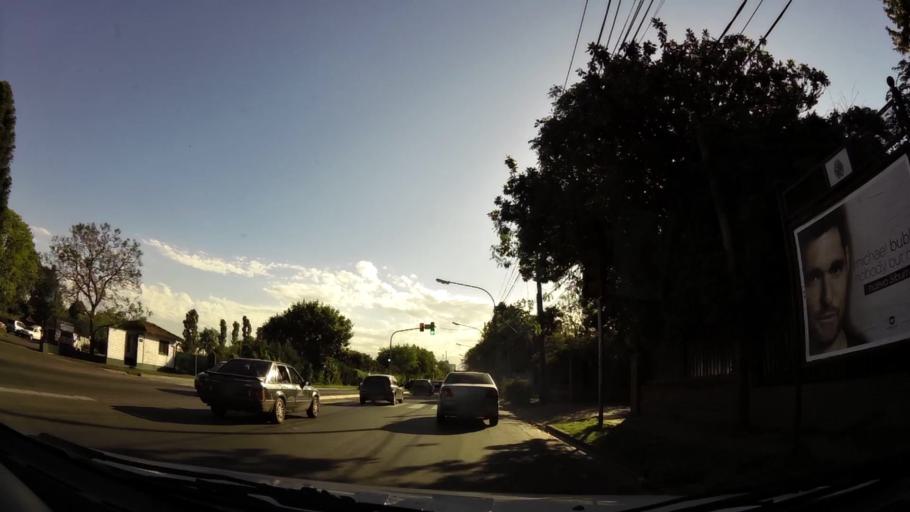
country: AR
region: Buenos Aires
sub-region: Partido de San Isidro
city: San Isidro
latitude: -34.4899
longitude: -58.5428
